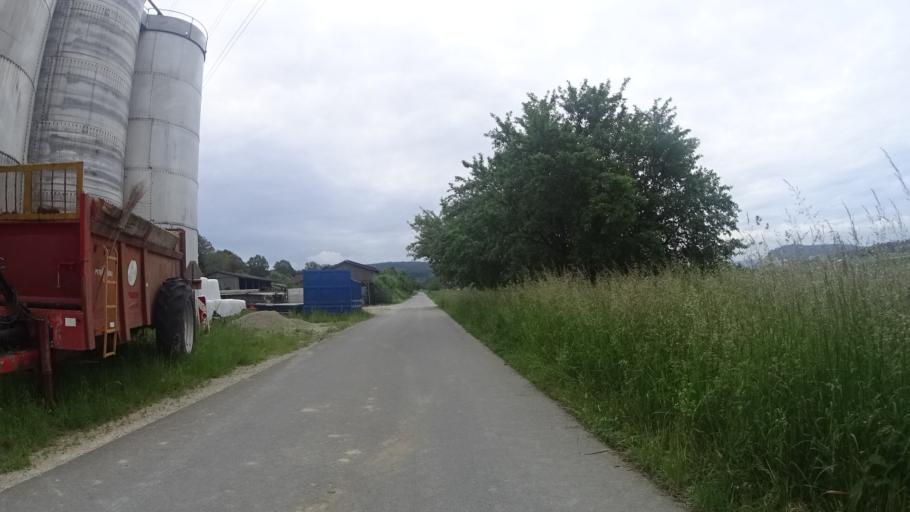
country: CH
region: Aargau
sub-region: Bezirk Baden
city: Wurenlingen
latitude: 47.5447
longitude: 8.2546
